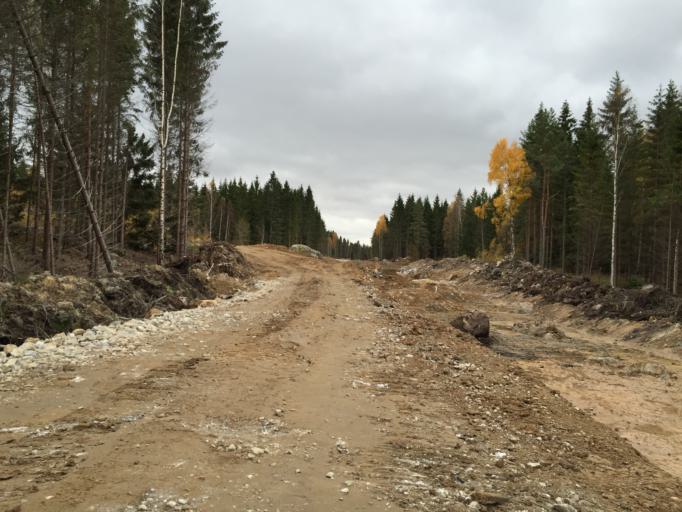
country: SE
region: Vaestmanland
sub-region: Hallstahammars Kommun
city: Hallstahammar
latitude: 59.6331
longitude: 16.2093
